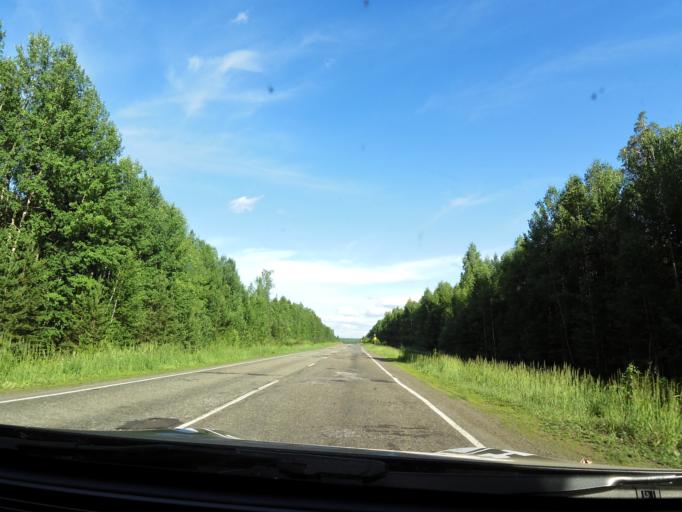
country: RU
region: Kirov
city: Dubrovka
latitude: 58.8965
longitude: 51.3224
